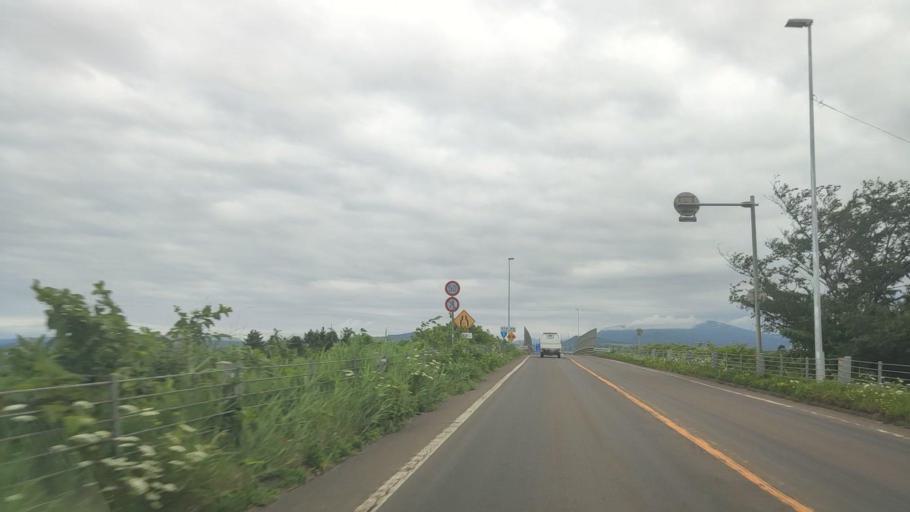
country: JP
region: Hokkaido
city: Nanae
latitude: 42.2830
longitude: 140.2718
